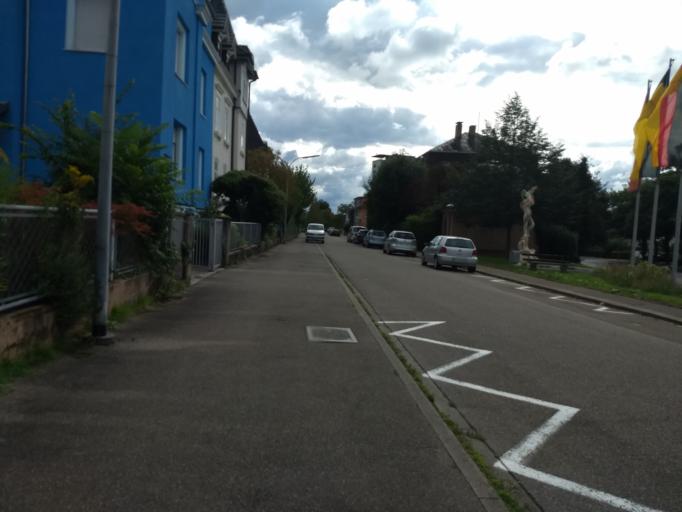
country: DE
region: Baden-Wuerttemberg
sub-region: Freiburg Region
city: Loerrach
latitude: 47.6001
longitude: 7.6581
